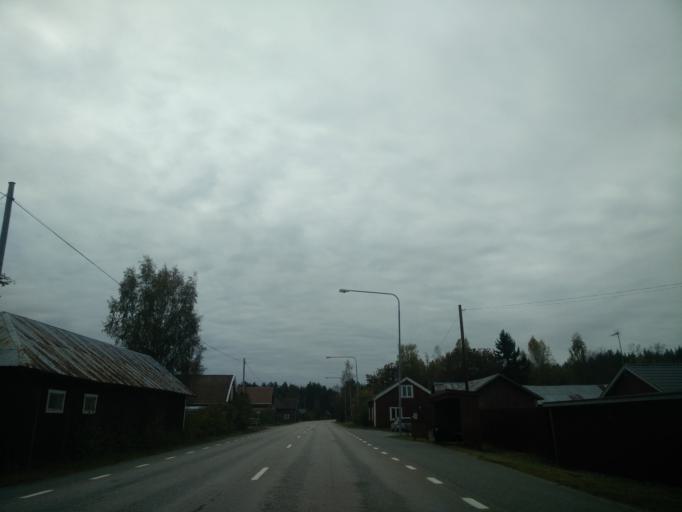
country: SE
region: Gaevleborg
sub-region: Gavle Kommun
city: Norrsundet
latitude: 60.8736
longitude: 17.1657
